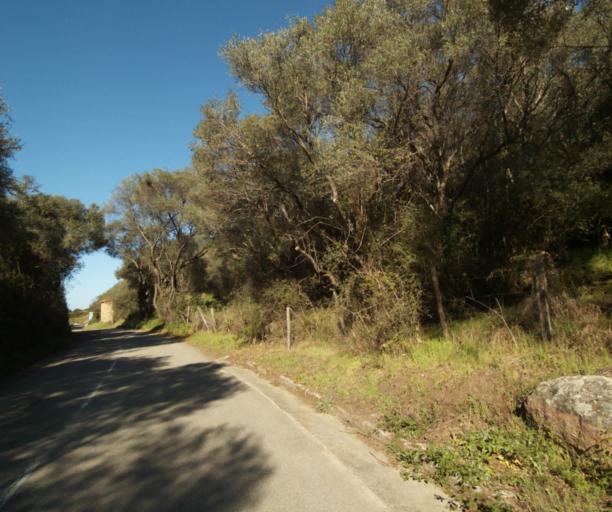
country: FR
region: Corsica
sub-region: Departement de la Corse-du-Sud
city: Propriano
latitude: 41.6651
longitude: 8.8892
